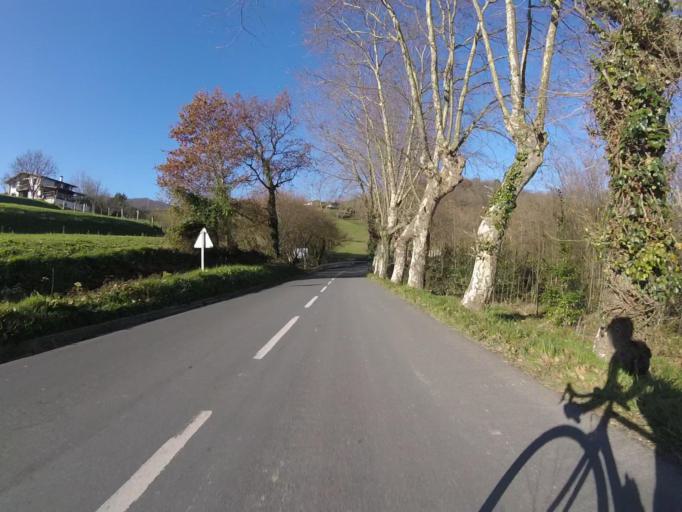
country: ES
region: Basque Country
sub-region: Provincia de Guipuzcoa
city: Fuenterrabia
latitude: 43.3657
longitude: -1.8075
